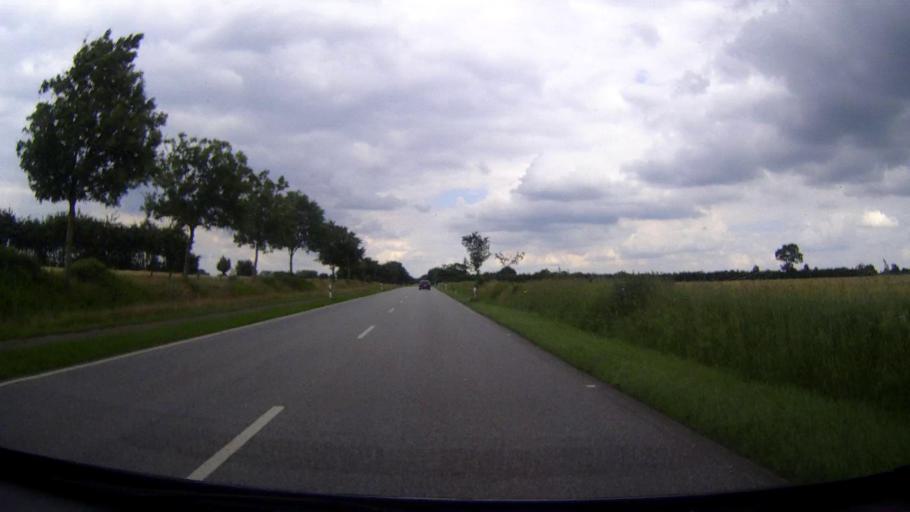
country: DE
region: Schleswig-Holstein
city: Christinenthal
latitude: 54.0592
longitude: 9.5516
